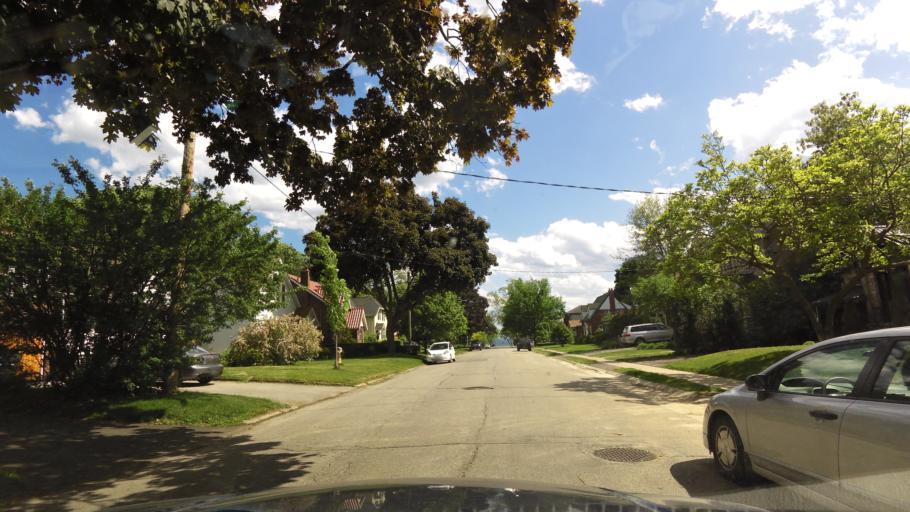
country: CA
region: Ontario
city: Etobicoke
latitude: 43.5909
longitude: -79.5357
